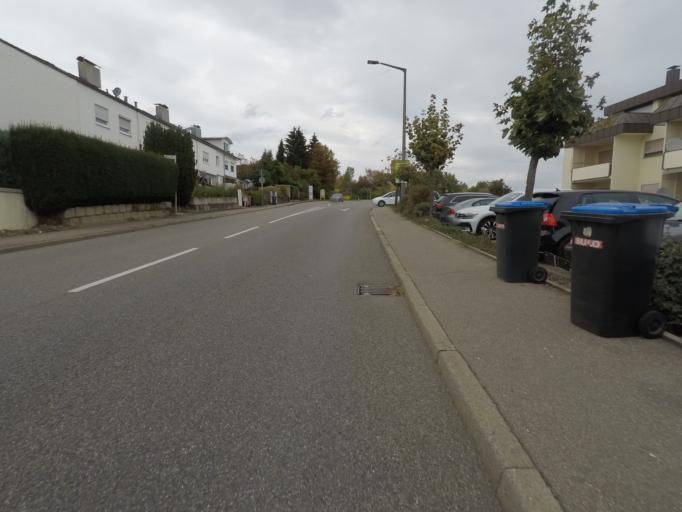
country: DE
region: Baden-Wuerttemberg
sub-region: Regierungsbezirk Stuttgart
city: Schlaitdorf
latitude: 48.6268
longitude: 9.2352
